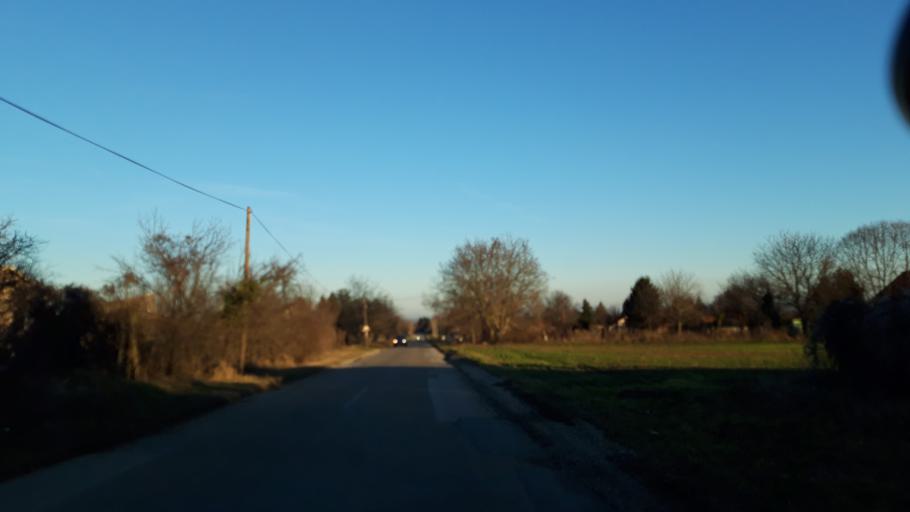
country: RS
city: Cortanovci
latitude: 45.1601
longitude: 19.9954
